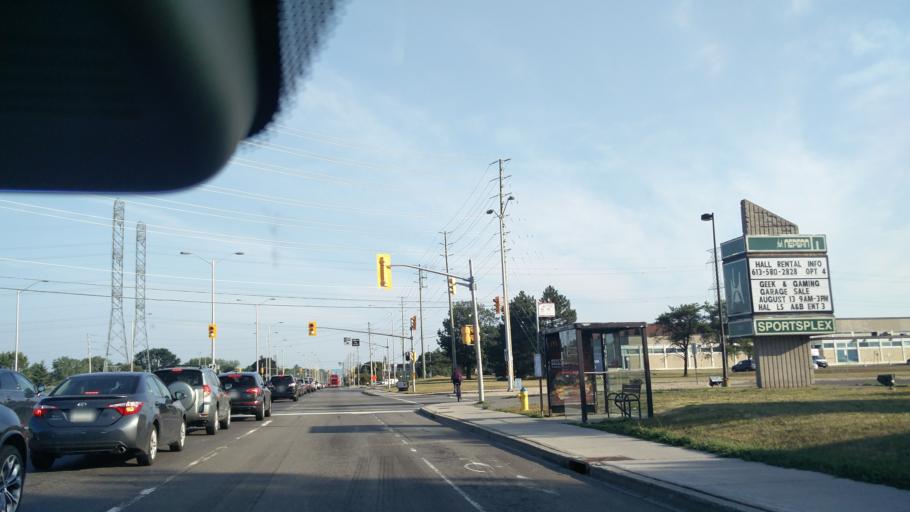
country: CA
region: Ontario
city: Bells Corners
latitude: 45.3267
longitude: -75.7475
